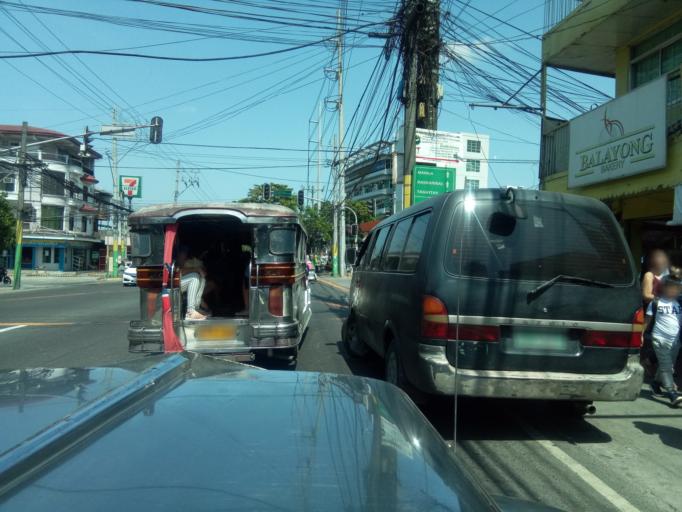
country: PH
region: Calabarzon
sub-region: Province of Cavite
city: Dasmarinas
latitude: 14.2937
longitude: 120.9383
